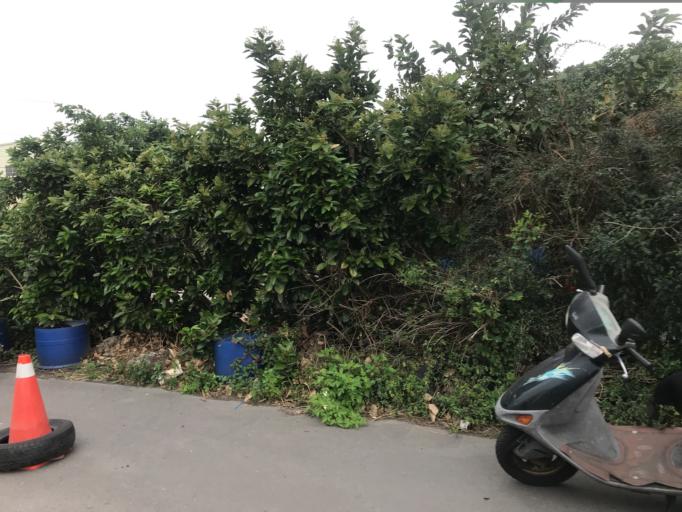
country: TW
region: Taiwan
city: Fengyuan
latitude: 24.3571
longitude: 120.6076
